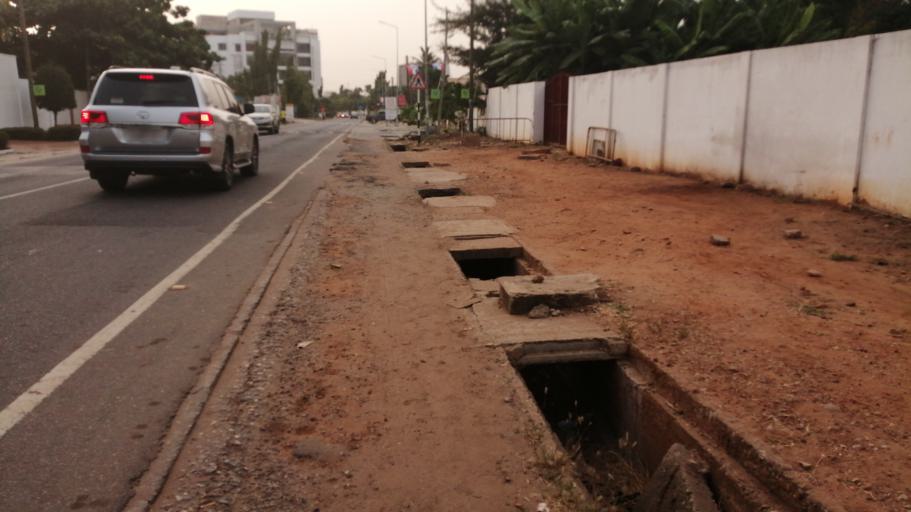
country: GH
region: Greater Accra
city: Medina Estates
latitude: 5.6193
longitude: -0.1779
